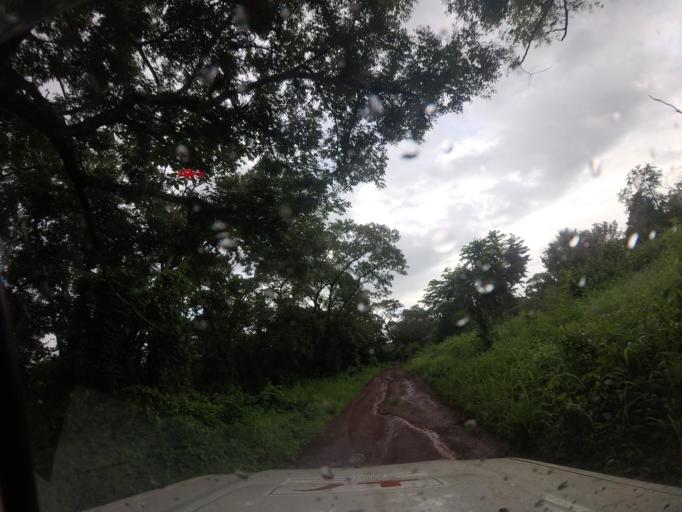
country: SL
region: Northern Province
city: Kamakwie
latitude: 9.7643
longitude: -12.3333
